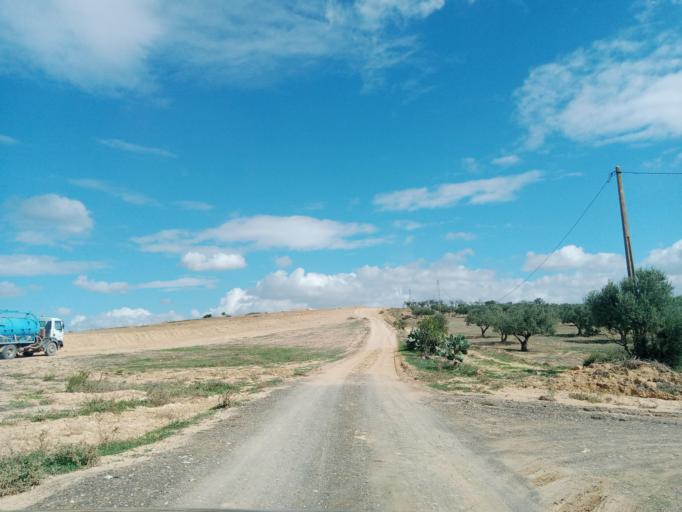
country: TN
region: Tunis
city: Oued Lill
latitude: 36.8068
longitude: 9.9862
